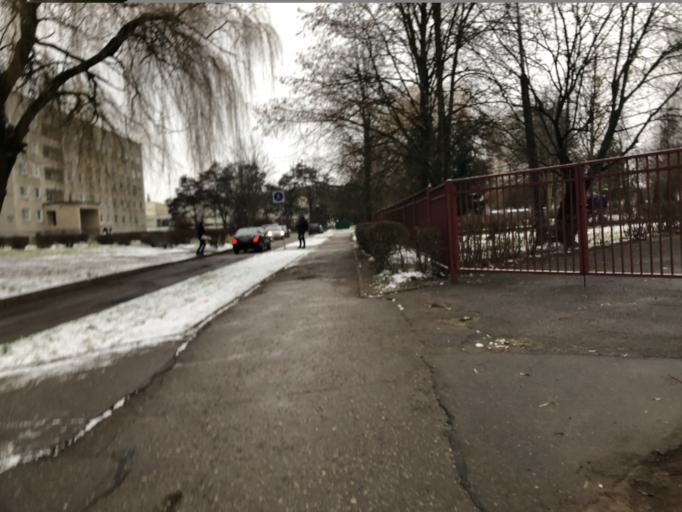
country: BY
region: Grodnenskaya
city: Hrodna
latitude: 53.7008
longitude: 23.8109
